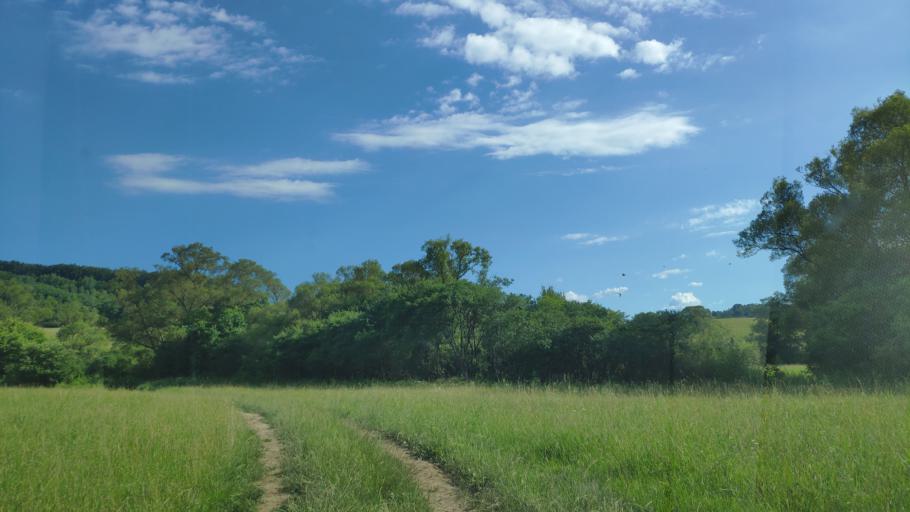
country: SK
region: Banskobystricky
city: Rimavska Sobota
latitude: 48.2494
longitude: 20.1061
